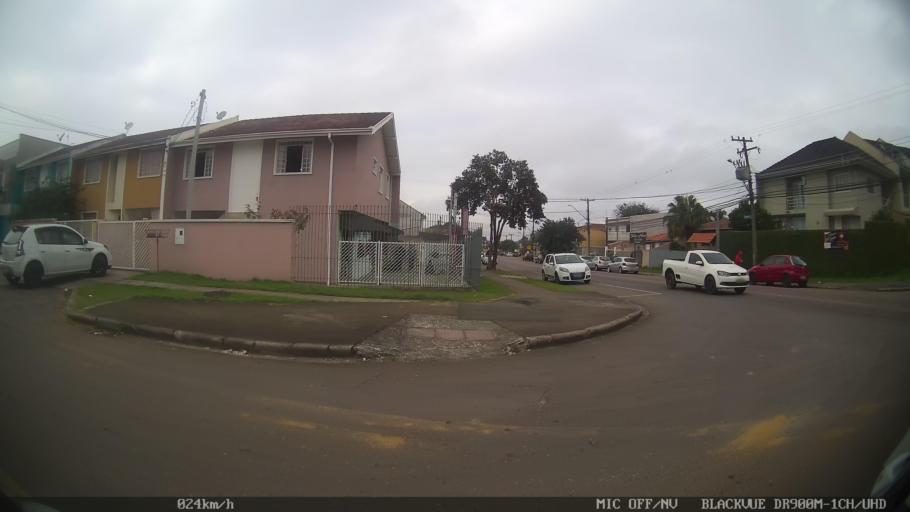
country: BR
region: Parana
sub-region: Almirante Tamandare
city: Almirante Tamandare
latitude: -25.3790
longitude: -49.3338
